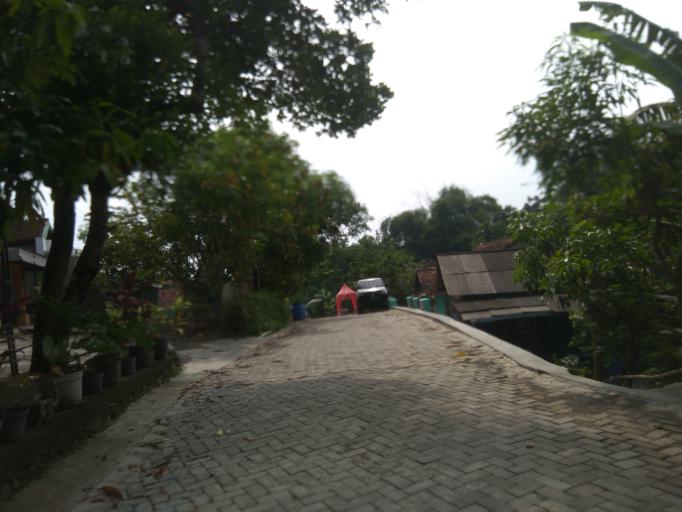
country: ID
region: Central Java
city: Semarang
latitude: -7.0355
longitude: 110.4097
